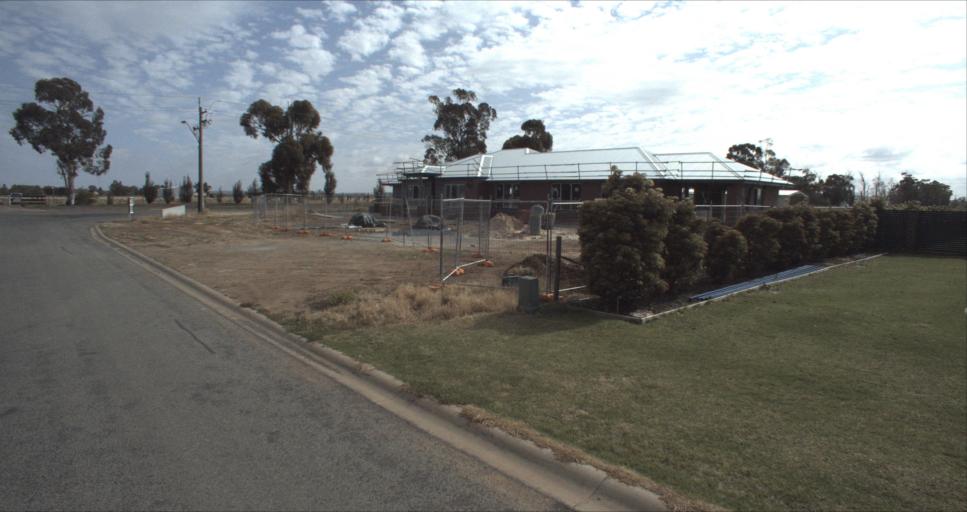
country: AU
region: New South Wales
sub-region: Leeton
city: Leeton
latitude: -34.5582
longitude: 146.4271
